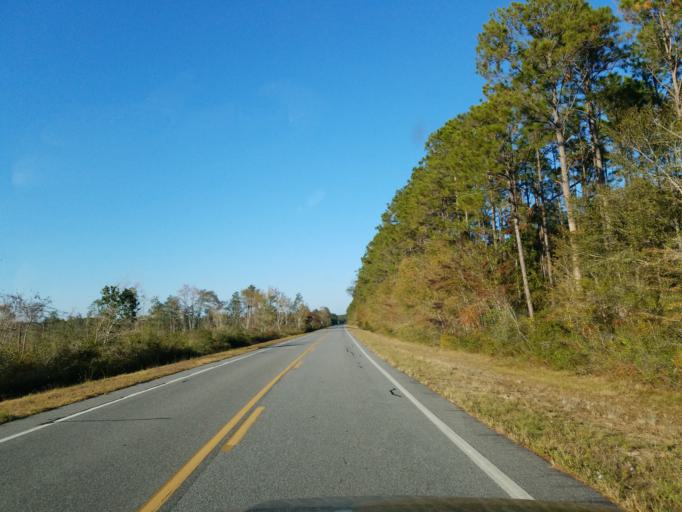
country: US
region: Georgia
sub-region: Echols County
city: Statenville
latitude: 30.8491
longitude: -83.0529
